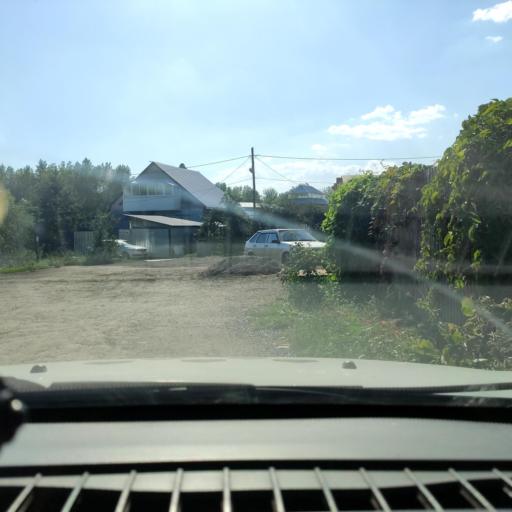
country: RU
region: Samara
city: Smyshlyayevka
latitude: 53.2067
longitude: 50.3283
